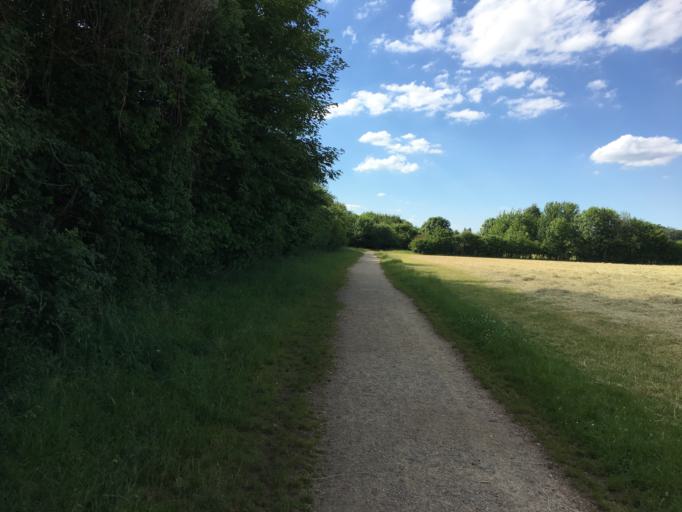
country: DE
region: North Rhine-Westphalia
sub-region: Regierungsbezirk Koln
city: Dueren
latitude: 50.7822
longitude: 6.4752
